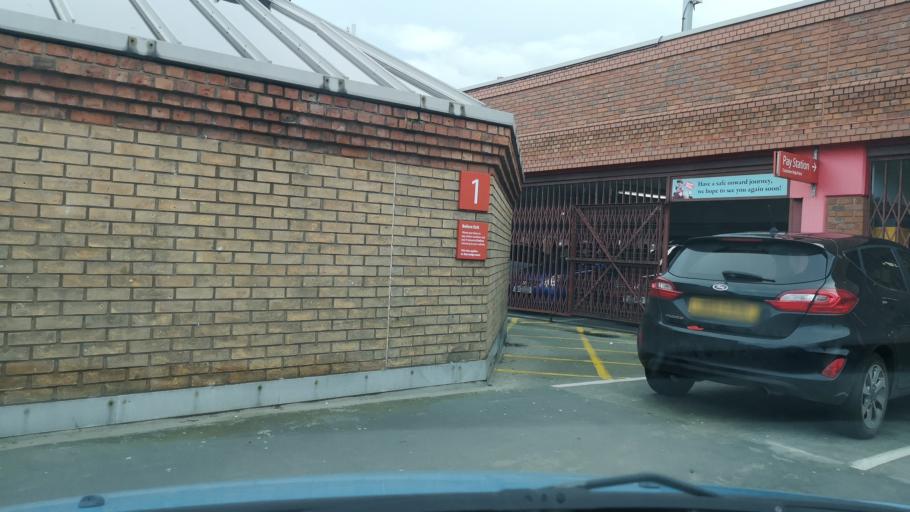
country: GB
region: England
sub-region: City and Borough of Wakefield
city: Wakefield
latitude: 53.6820
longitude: -1.4979
